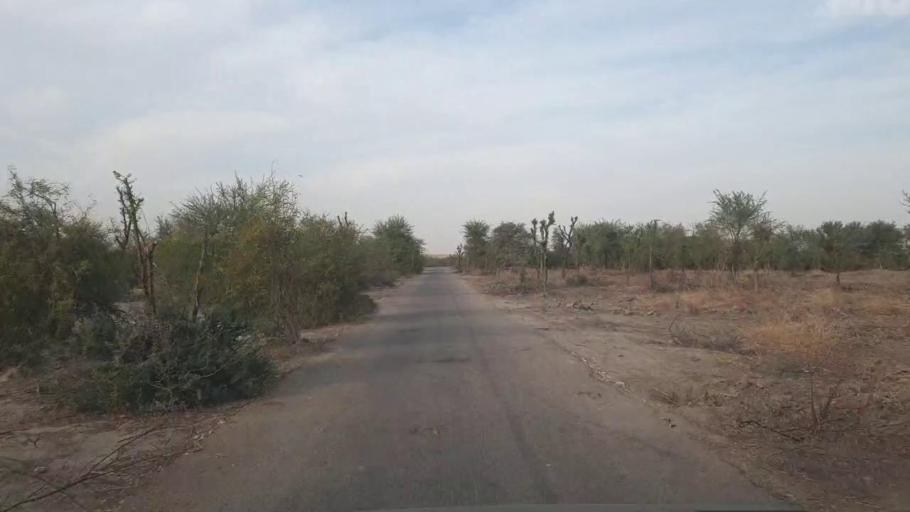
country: PK
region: Sindh
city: Nabisar
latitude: 25.1102
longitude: 69.6777
